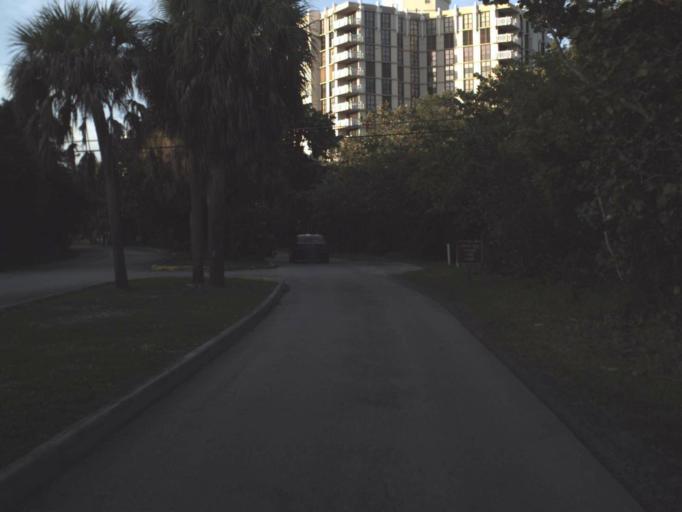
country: US
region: Florida
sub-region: Miami-Dade County
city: Key Biscayne
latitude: 25.6815
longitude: -80.1574
